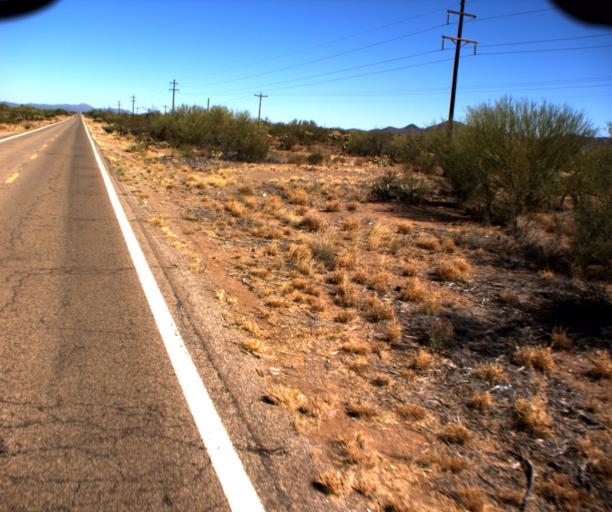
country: US
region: Arizona
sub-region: Pima County
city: Sells
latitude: 31.9975
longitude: -111.9832
